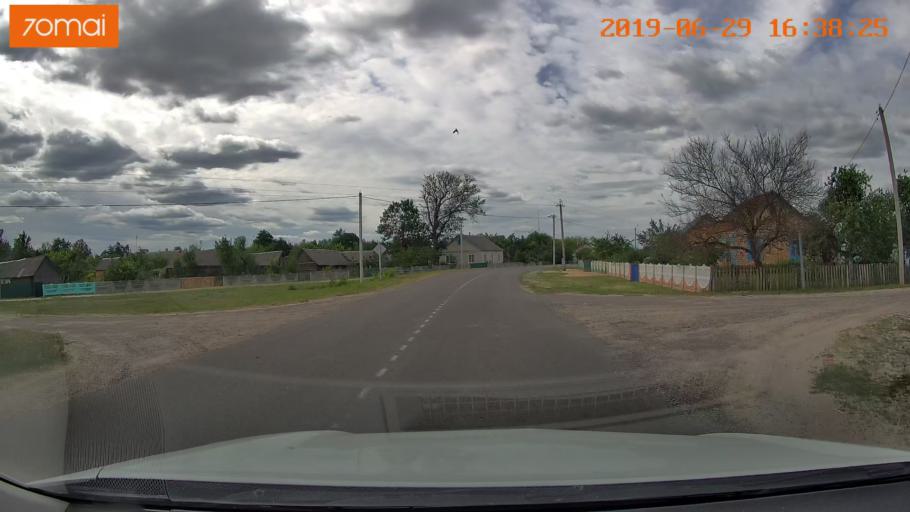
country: BY
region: Brest
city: Luninyets
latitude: 52.2326
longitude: 27.0159
